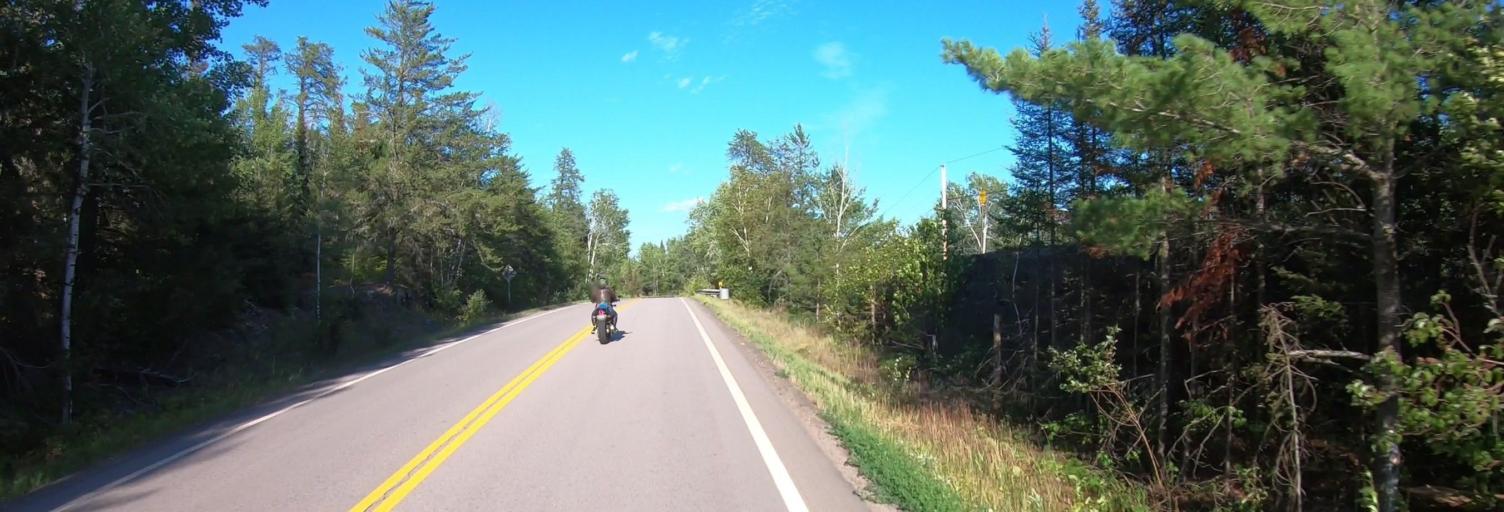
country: US
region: Minnesota
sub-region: Saint Louis County
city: Ely
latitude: 47.9591
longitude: -91.5492
